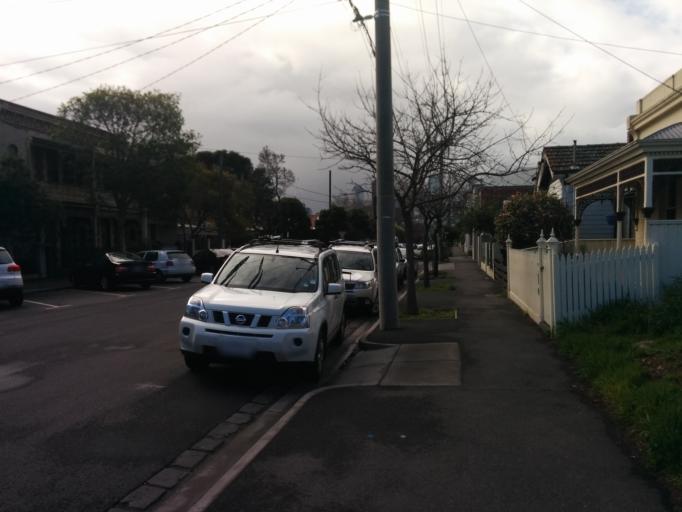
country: AU
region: Victoria
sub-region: Port Phillip
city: Port Melbourne
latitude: -37.8357
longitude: 144.9434
